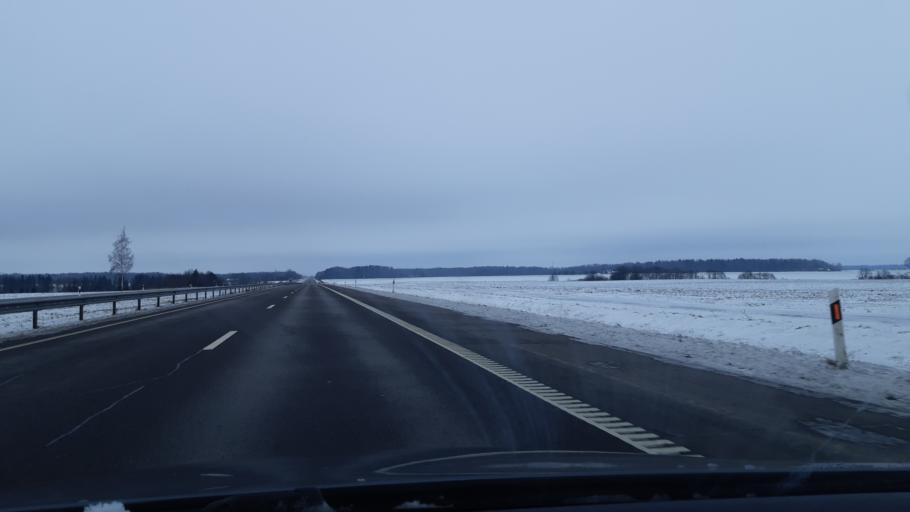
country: LT
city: Vilkija
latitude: 55.1168
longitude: 23.7631
